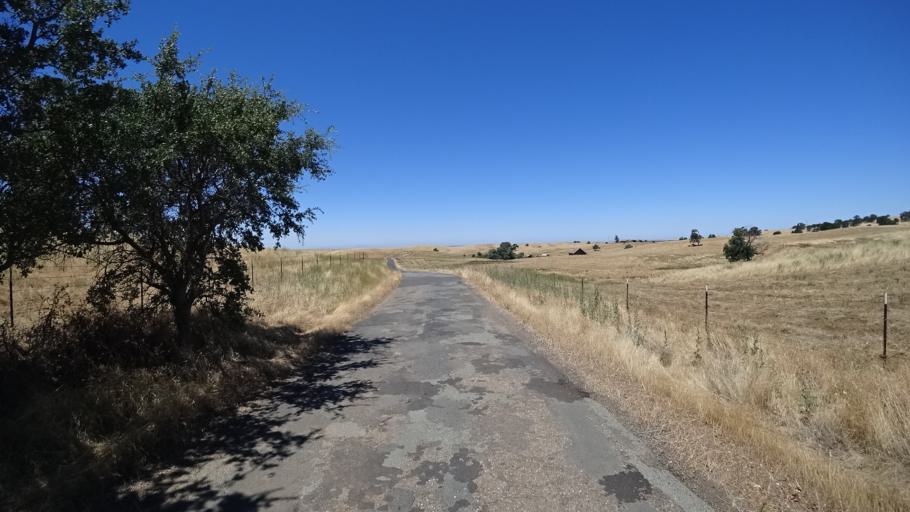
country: US
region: California
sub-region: Calaveras County
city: Rancho Calaveras
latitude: 38.0465
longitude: -120.8277
